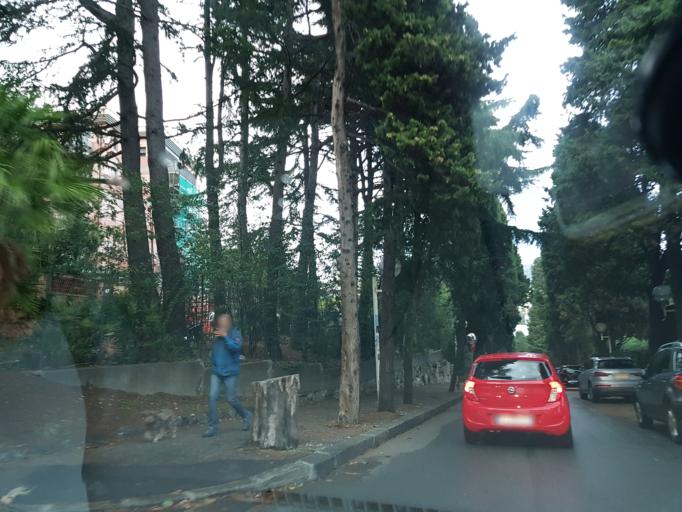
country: IT
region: Liguria
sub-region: Provincia di Genova
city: Genoa
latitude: 44.3992
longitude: 8.9696
